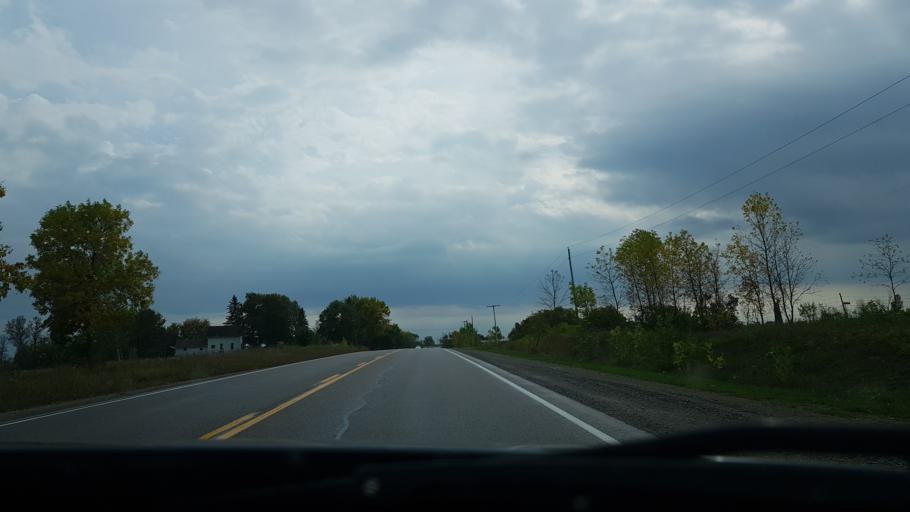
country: CA
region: Ontario
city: Omemee
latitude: 44.4512
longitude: -78.7687
